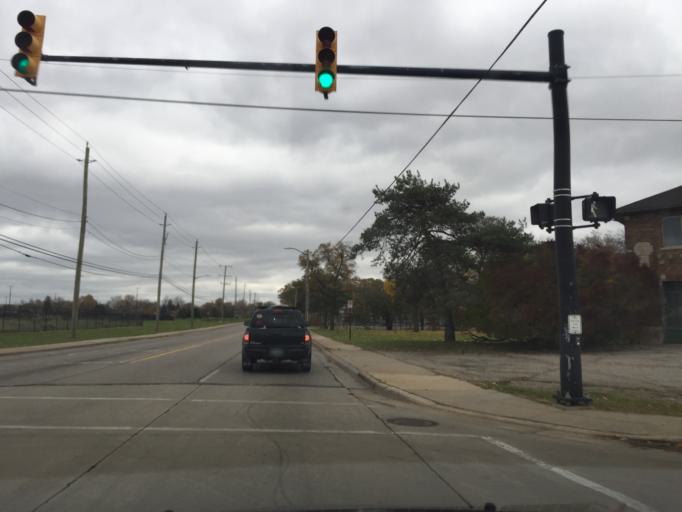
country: US
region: Michigan
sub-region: Oakland County
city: Pontiac
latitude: 42.6562
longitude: -83.2860
